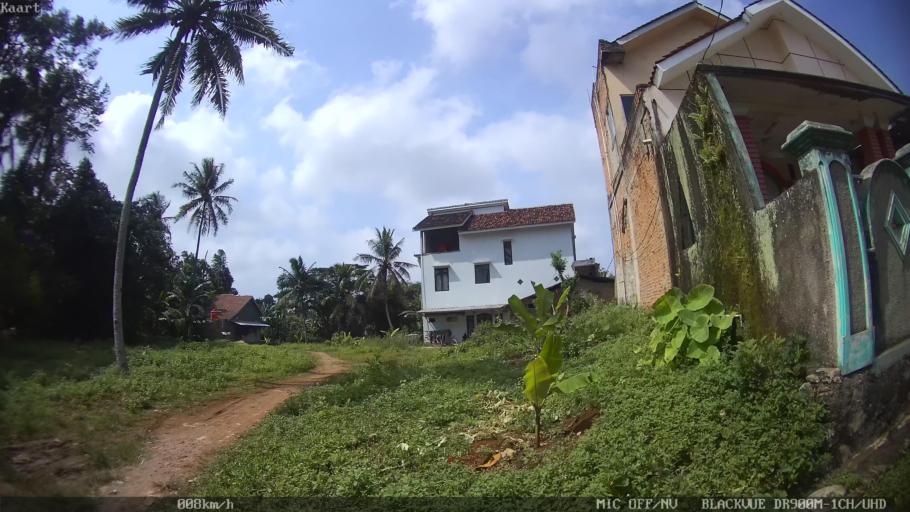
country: ID
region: Lampung
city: Kedaton
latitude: -5.3305
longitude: 105.2829
